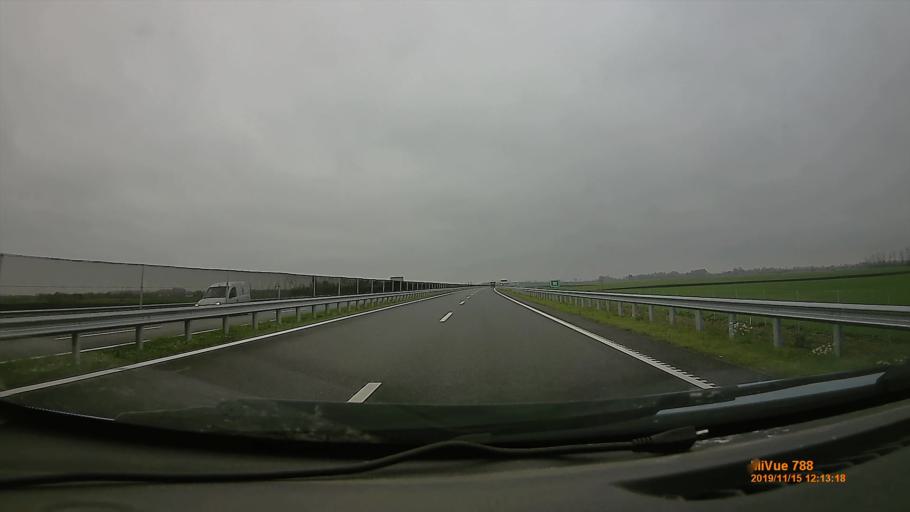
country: HU
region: Bekes
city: Bekesszentandras
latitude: 46.8251
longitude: 20.4905
